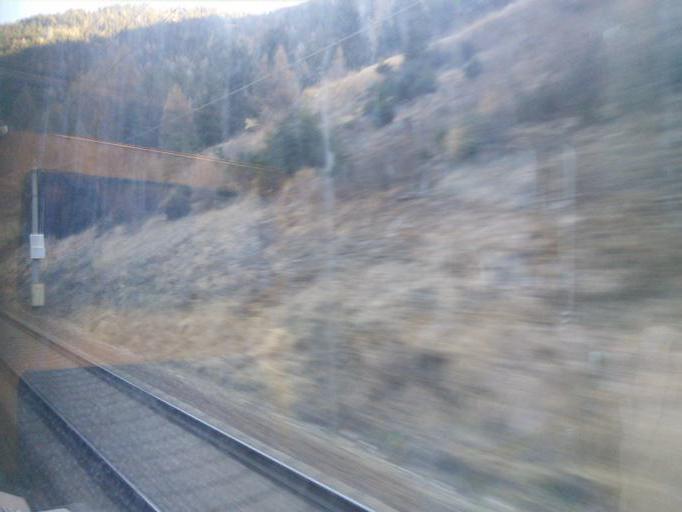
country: AT
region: Tyrol
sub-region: Politischer Bezirk Innsbruck Land
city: Gries am Brenner
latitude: 47.0683
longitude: 11.4867
